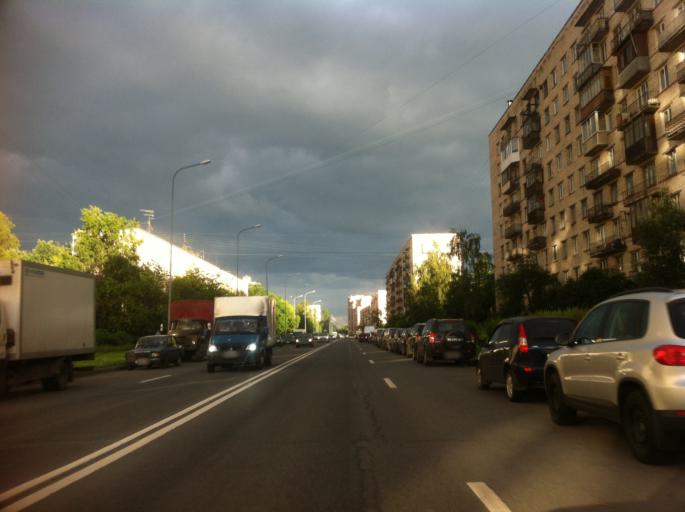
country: RU
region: St.-Petersburg
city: Dachnoye
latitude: 59.8470
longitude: 30.2295
